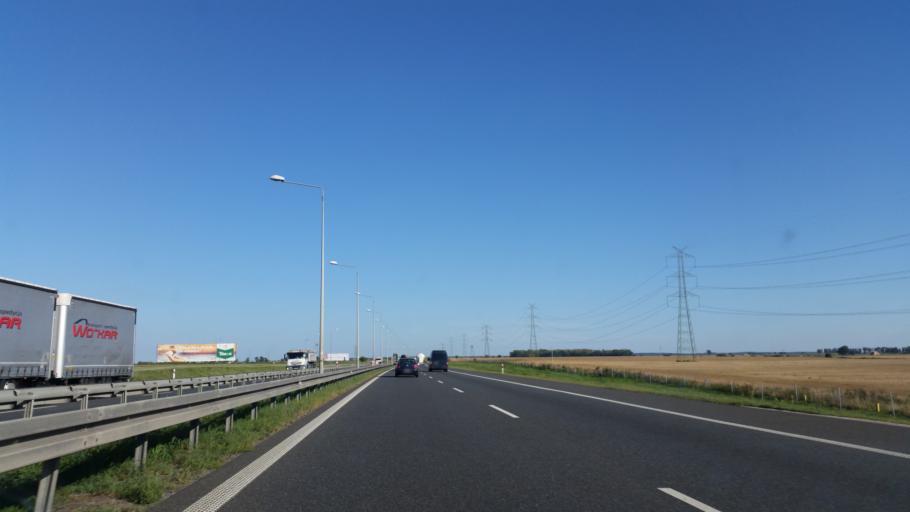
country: PL
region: Opole Voivodeship
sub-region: Powiat brzeski
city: Olszanka
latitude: 50.7565
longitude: 17.4309
